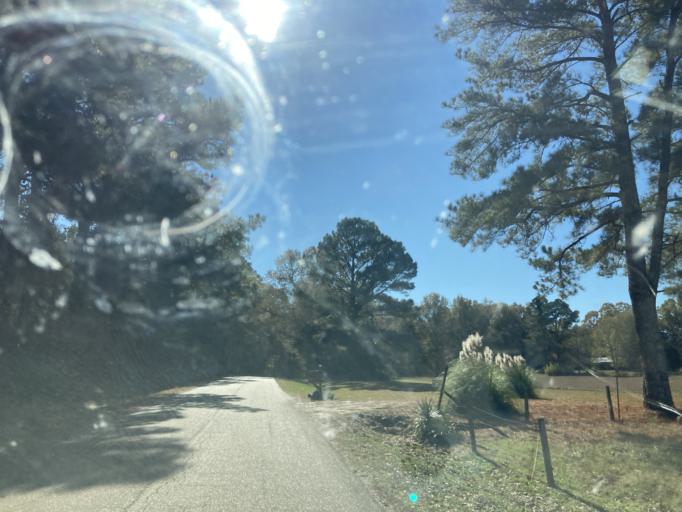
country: US
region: Mississippi
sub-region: Hinds County
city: Lynchburg
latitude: 32.5809
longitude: -90.5696
